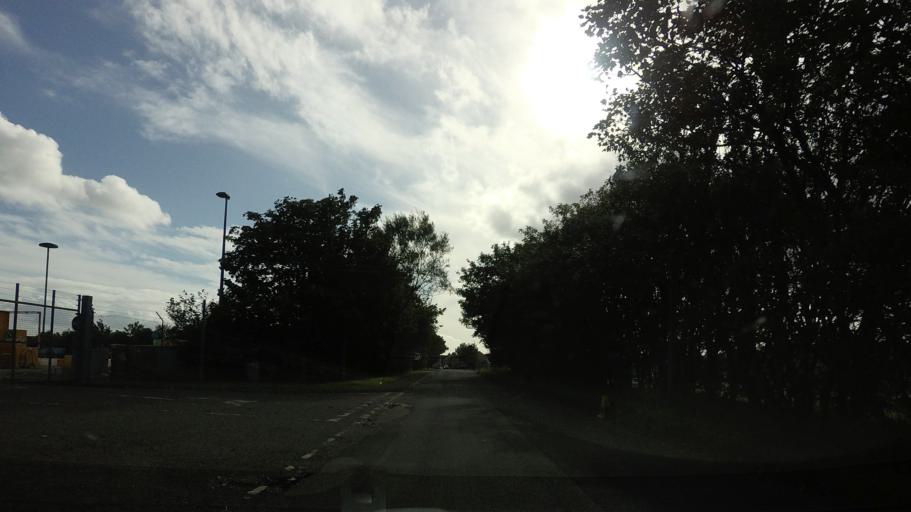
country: GB
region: Scotland
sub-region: Highland
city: Wick
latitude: 58.4498
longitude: -3.0881
